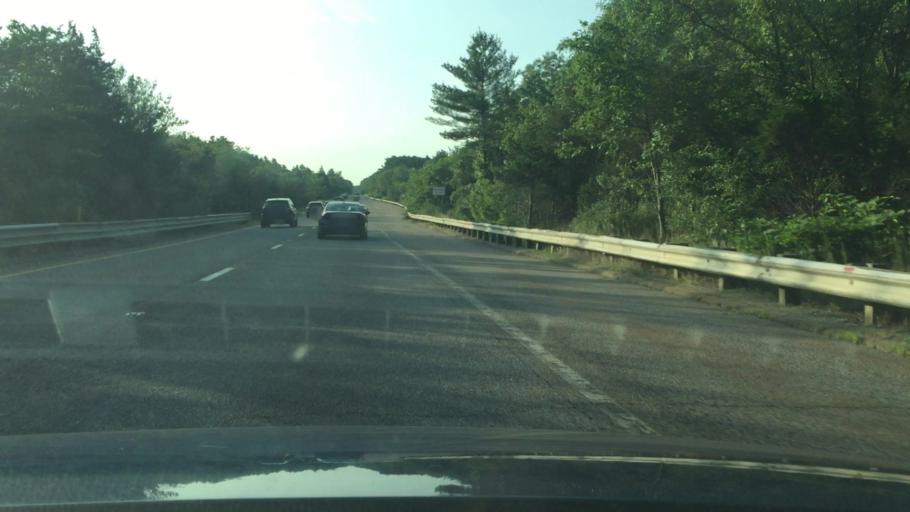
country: US
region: Massachusetts
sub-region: Plymouth County
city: Hanover
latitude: 42.1422
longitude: -70.8286
